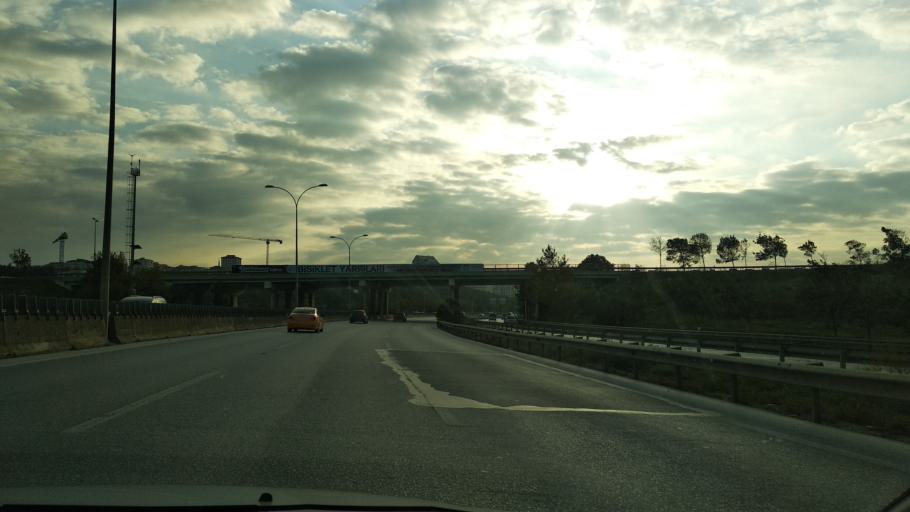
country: TR
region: Istanbul
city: Icmeler
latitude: 40.8797
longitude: 29.3151
